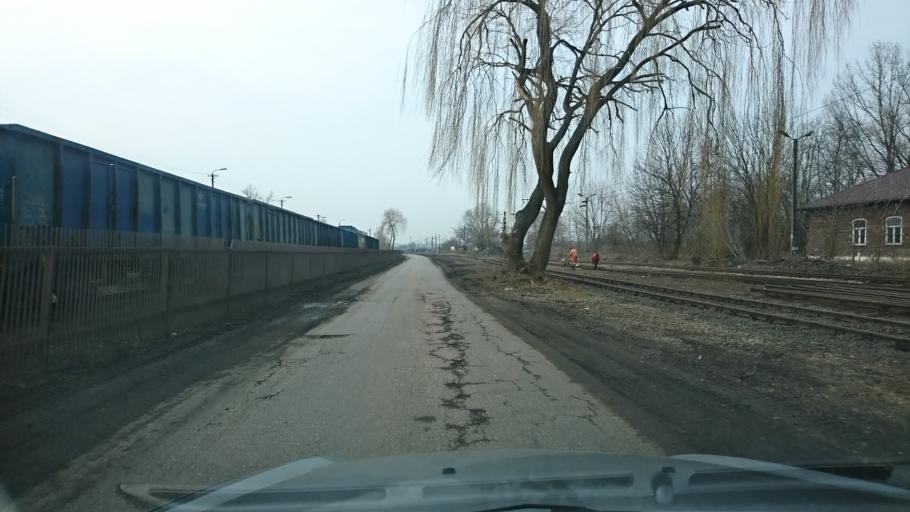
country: PL
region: Lesser Poland Voivodeship
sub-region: Powiat wielicki
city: Czarnochowice
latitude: 50.0249
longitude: 20.0215
